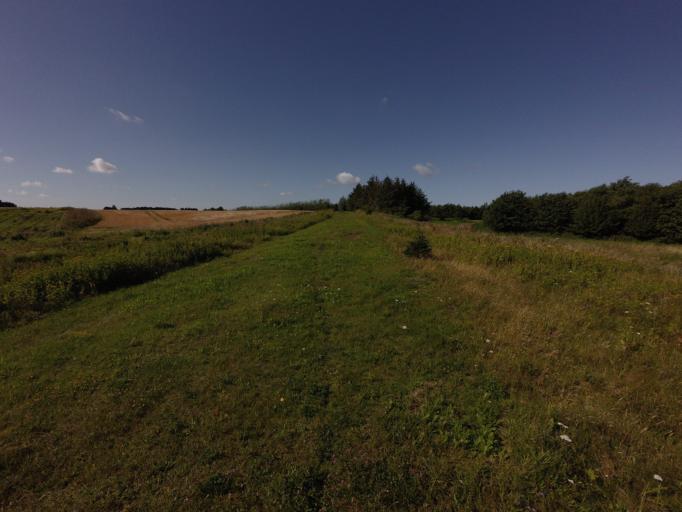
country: DK
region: North Denmark
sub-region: Hjorring Kommune
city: Vra
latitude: 57.3994
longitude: 9.7996
